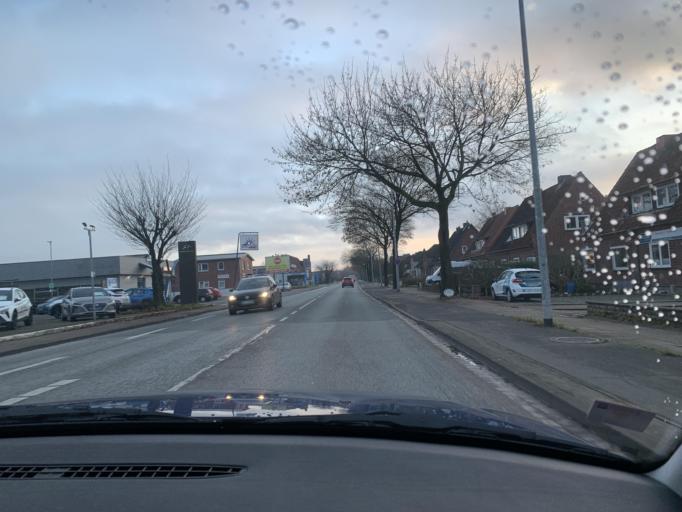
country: DE
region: Schleswig-Holstein
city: Heide
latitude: 54.1857
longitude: 9.0901
